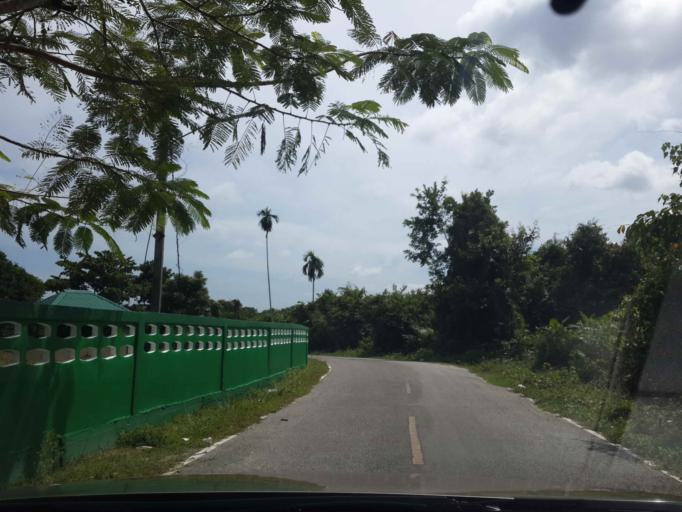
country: TH
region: Narathiwat
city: Rueso
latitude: 6.3997
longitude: 101.5155
